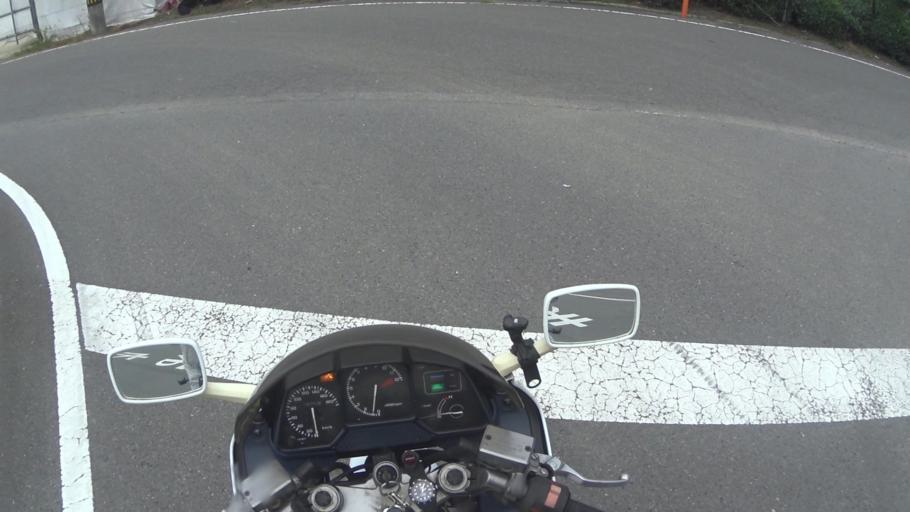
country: JP
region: Kyoto
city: Uji
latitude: 34.8382
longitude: 135.8589
